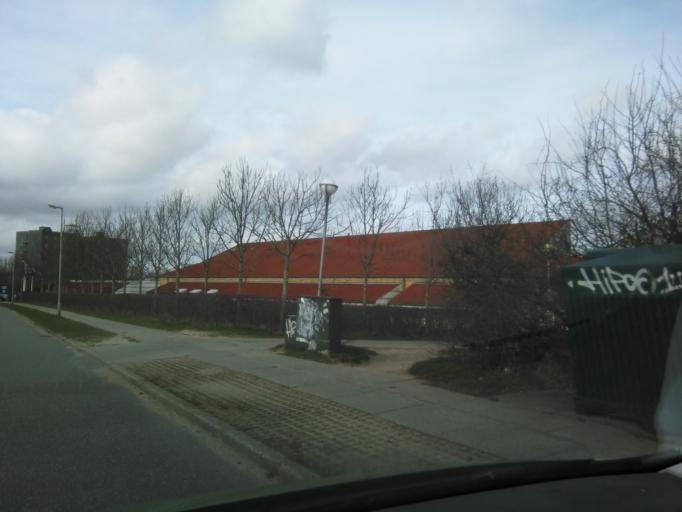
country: DK
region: Central Jutland
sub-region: Arhus Kommune
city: Arhus
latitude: 56.1931
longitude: 10.1932
